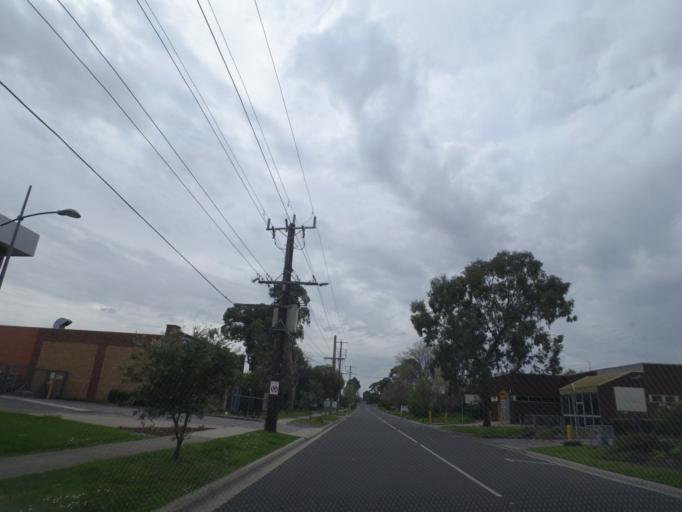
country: AU
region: Victoria
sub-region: Knox
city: Bayswater
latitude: -37.8466
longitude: 145.2785
